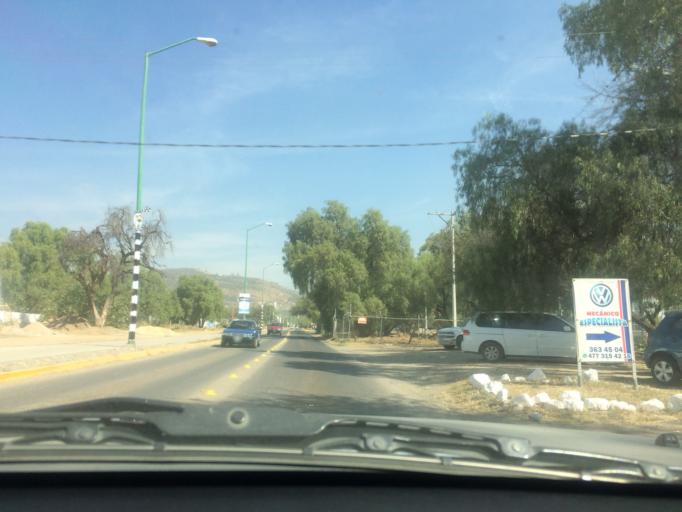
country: MX
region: Guanajuato
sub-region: Leon
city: Medina
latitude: 21.1762
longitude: -101.6538
